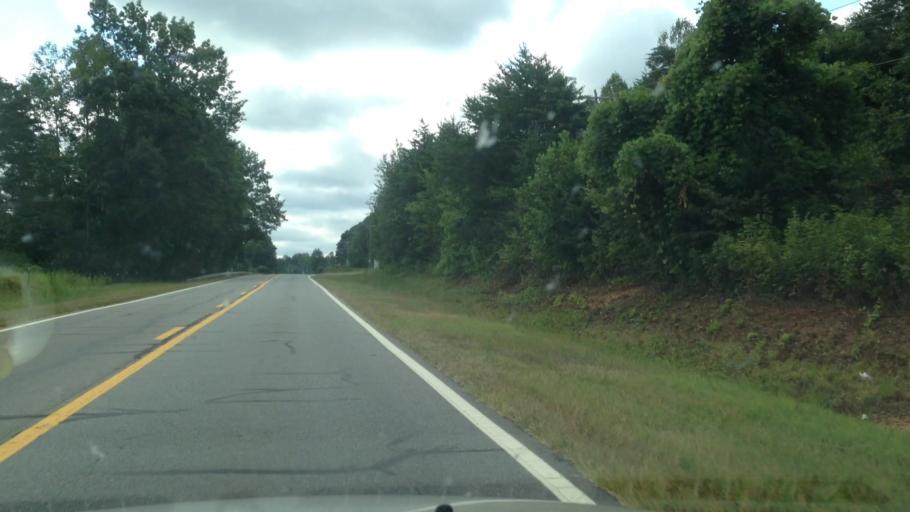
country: US
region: North Carolina
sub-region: Rockingham County
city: Wentworth
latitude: 36.3784
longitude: -79.8572
